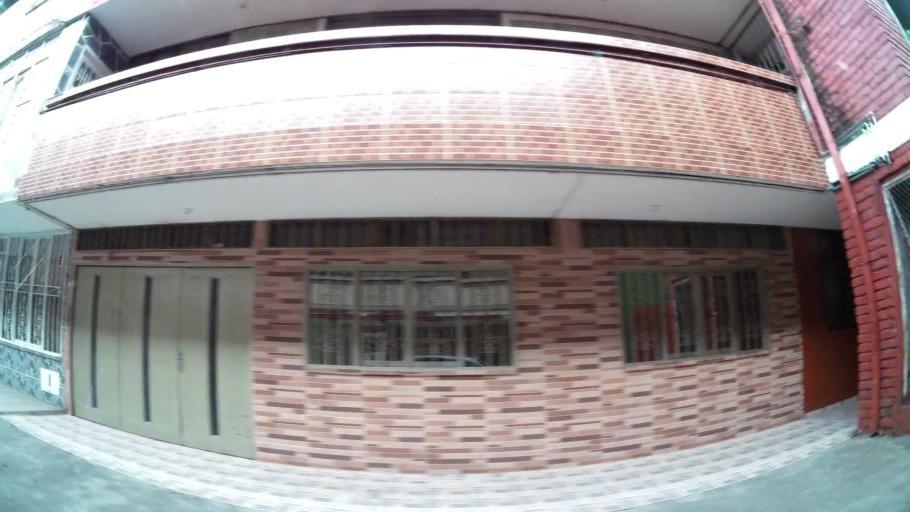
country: CO
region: Valle del Cauca
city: Cali
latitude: 3.4690
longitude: -76.5162
